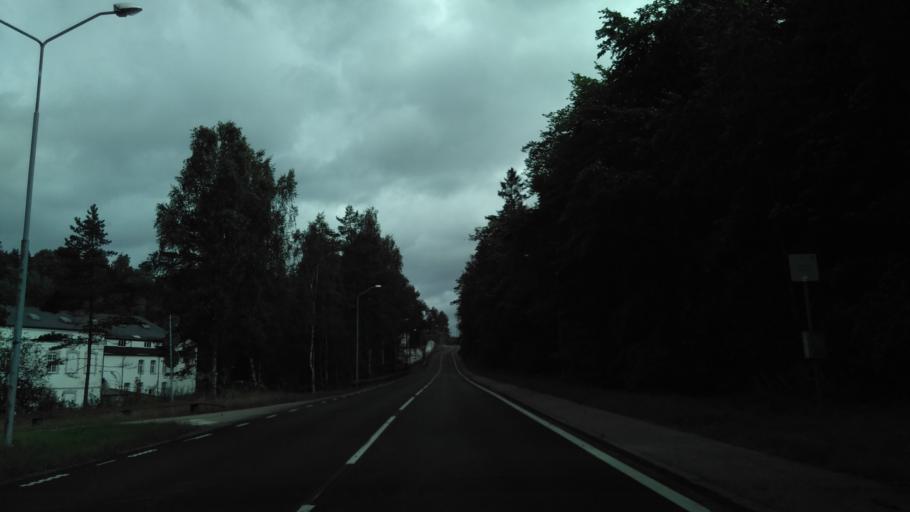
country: SE
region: Vaestra Goetaland
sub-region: Boras Kommun
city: Viskafors
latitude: 57.6251
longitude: 12.8379
